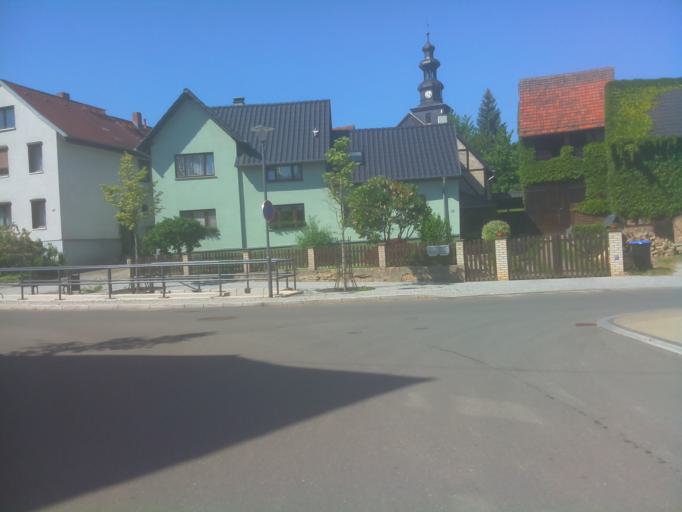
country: DE
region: Thuringia
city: Rudolstadt
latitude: 50.7110
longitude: 11.3468
